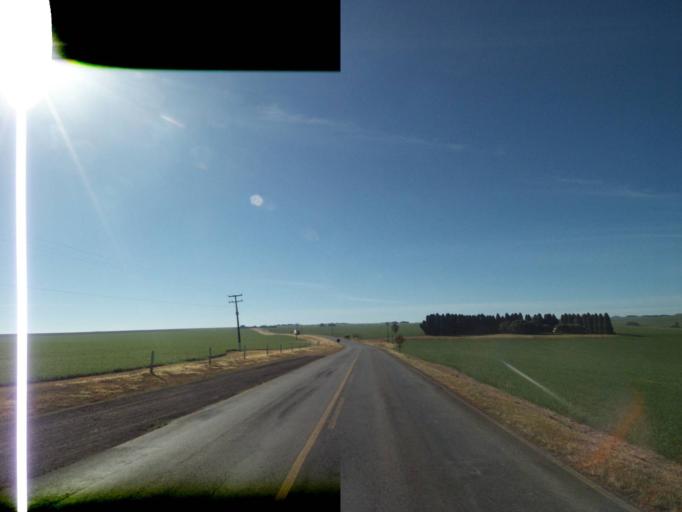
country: BR
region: Parana
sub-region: Tibagi
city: Tibagi
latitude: -24.5227
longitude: -50.3570
